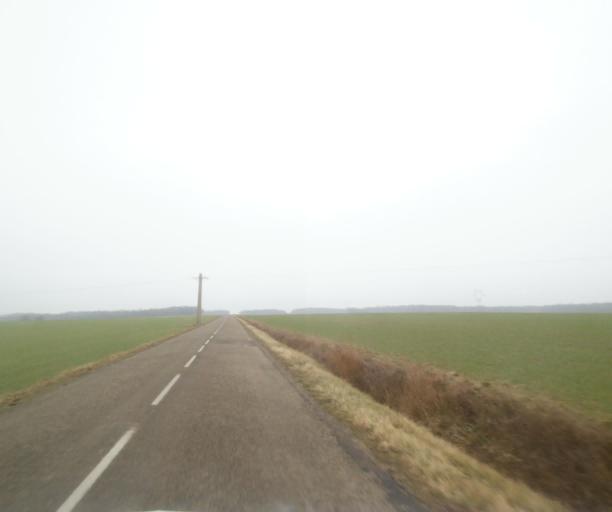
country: FR
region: Champagne-Ardenne
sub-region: Departement de la Haute-Marne
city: Bienville
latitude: 48.5223
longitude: 5.0445
